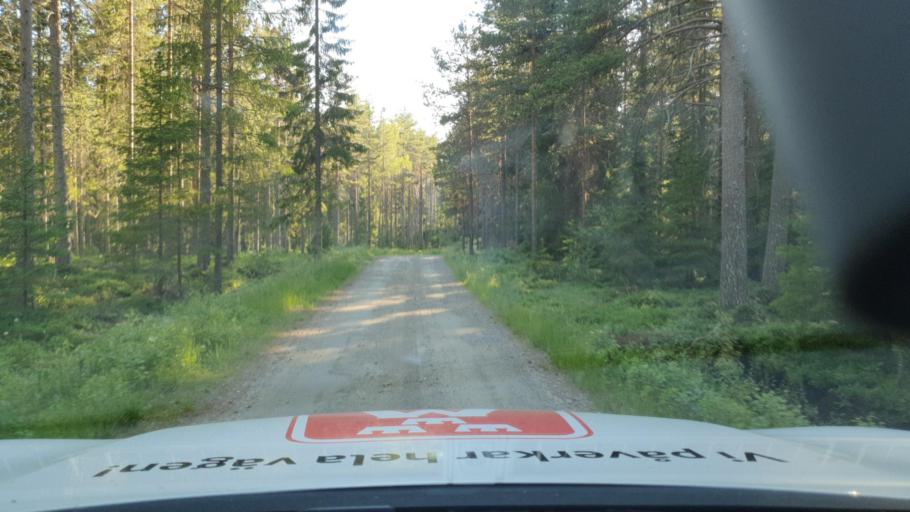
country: SE
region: Vaesterbotten
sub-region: Skelleftea Kommun
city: Skelleftehamn
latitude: 64.5260
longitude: 21.4851
